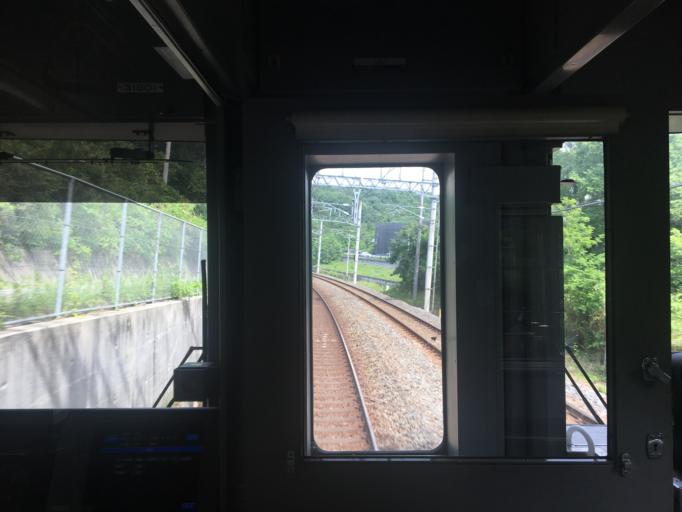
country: JP
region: Saitama
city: Ogawa
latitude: 36.0514
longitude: 139.3071
